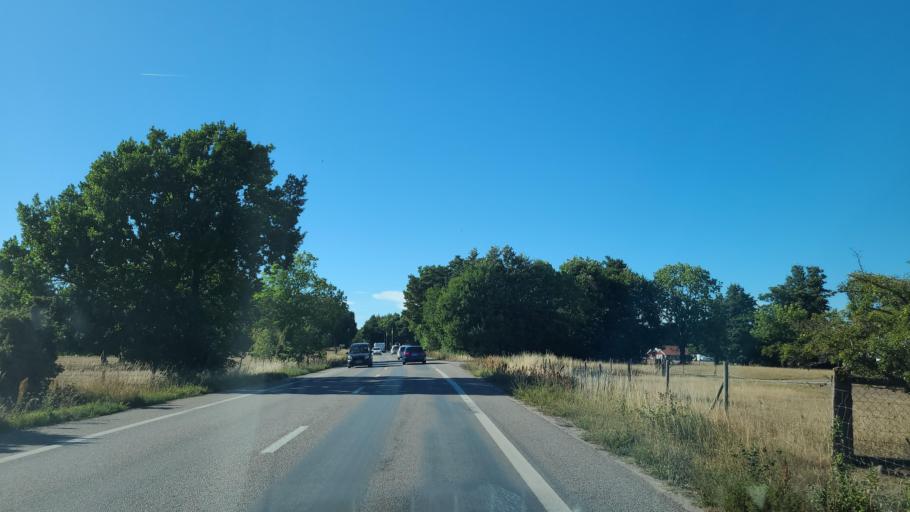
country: SE
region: Kalmar
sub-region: Borgholms Kommun
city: Borgholm
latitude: 57.2539
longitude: 17.0522
